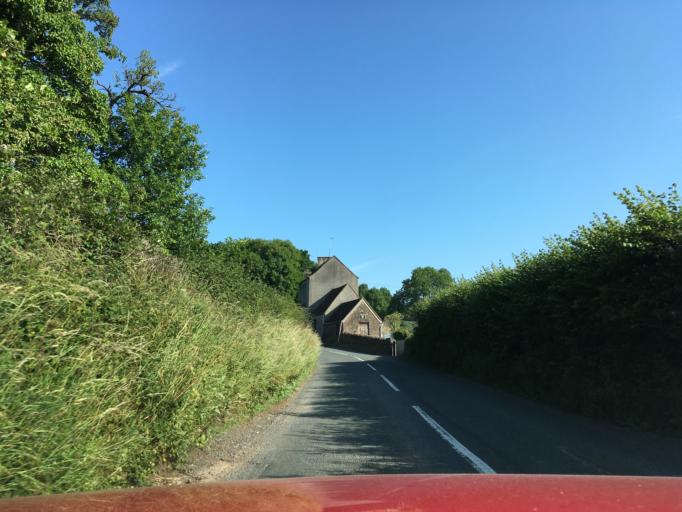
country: GB
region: England
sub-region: Gloucestershire
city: Lydney
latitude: 51.7661
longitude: -2.4828
